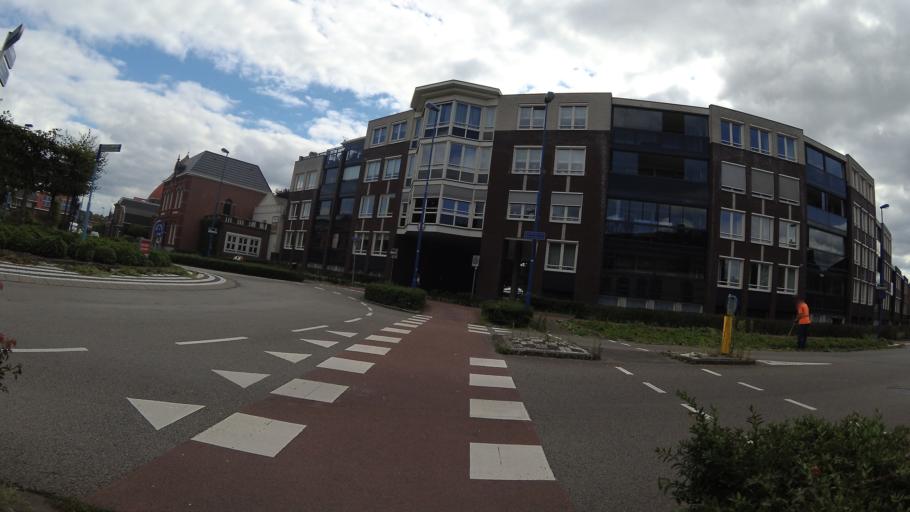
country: NL
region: North Brabant
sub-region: Gemeente Dongen
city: Dongen
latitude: 51.6281
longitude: 4.9355
